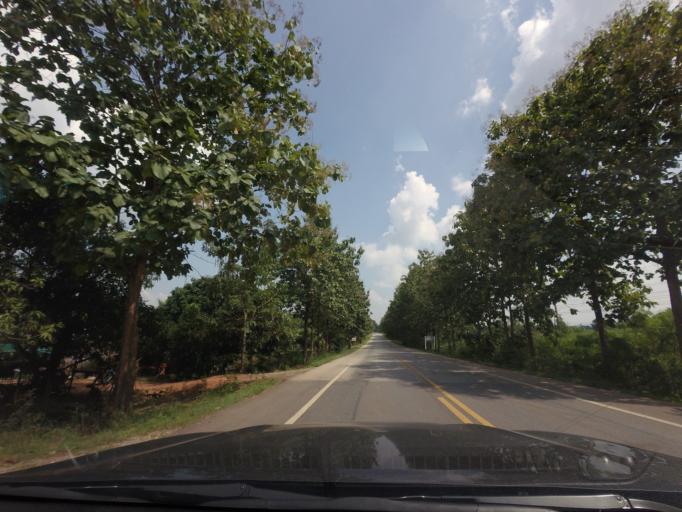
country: TH
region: Phitsanulok
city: Chat Trakan
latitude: 17.2831
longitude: 100.5276
